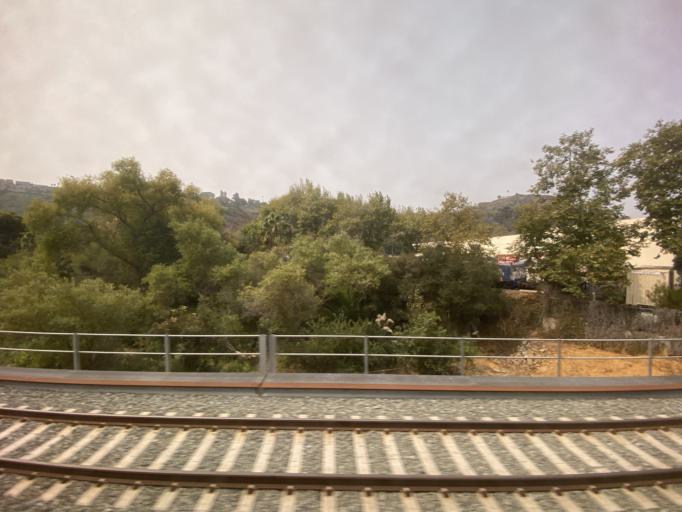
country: US
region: California
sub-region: San Diego County
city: La Jolla
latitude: 32.8294
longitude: -117.2307
